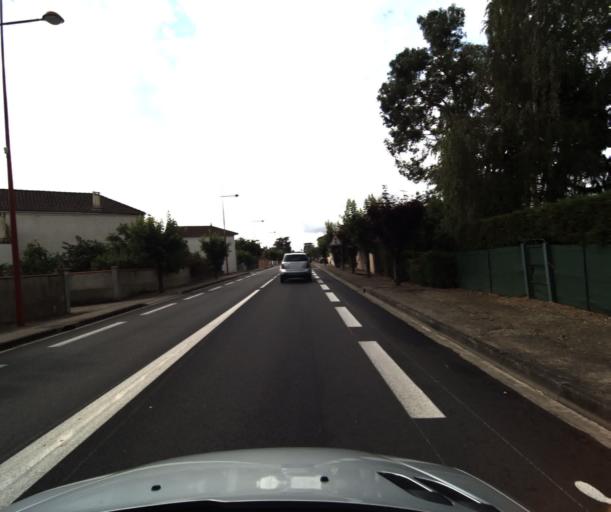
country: FR
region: Midi-Pyrenees
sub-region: Departement du Tarn-et-Garonne
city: Castelsarrasin
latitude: 44.0471
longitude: 1.1031
